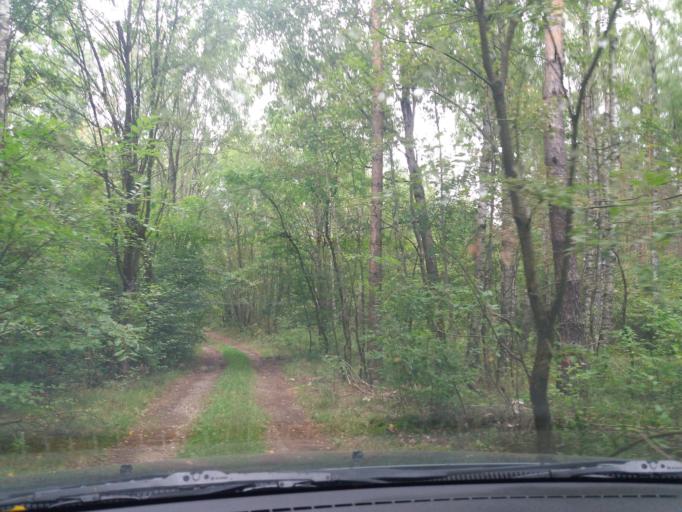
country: PL
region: Masovian Voivodeship
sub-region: Powiat mlawski
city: Wieczfnia Koscielna
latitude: 53.2318
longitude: 20.4798
